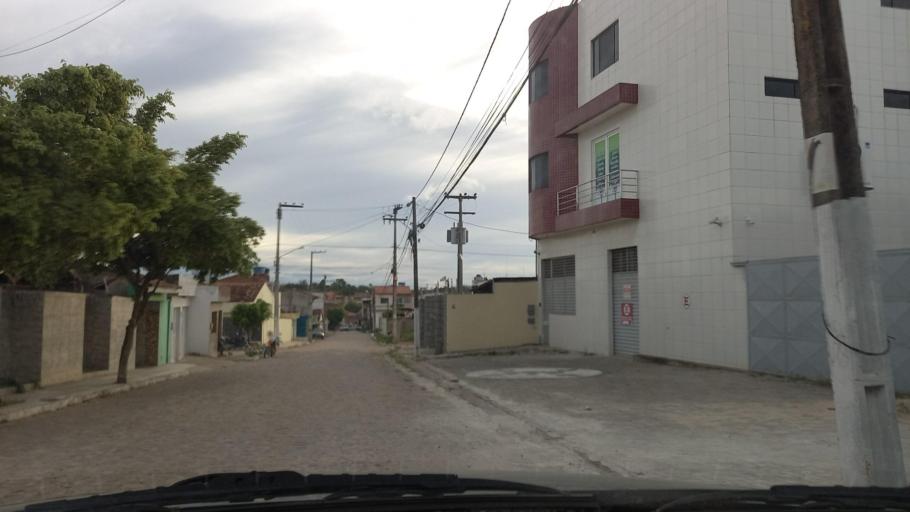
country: BR
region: Pernambuco
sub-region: Gravata
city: Gravata
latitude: -8.1950
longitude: -35.5744
